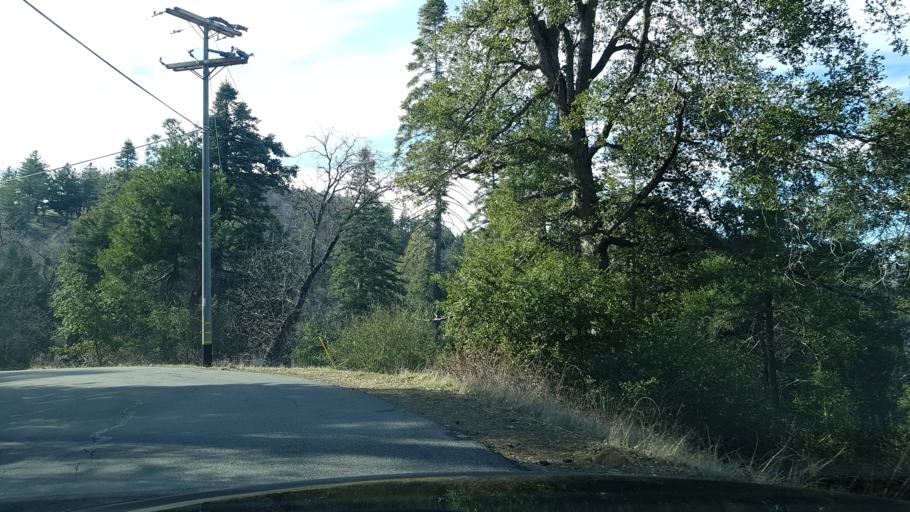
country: US
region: California
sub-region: Riverside County
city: Aguanga
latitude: 33.3331
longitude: -116.9077
